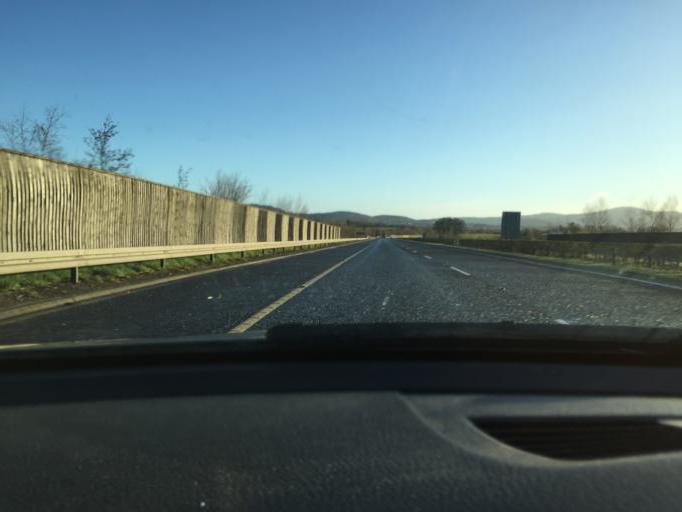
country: IE
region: Leinster
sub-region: Lu
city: Dundalk
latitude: 54.0264
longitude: -6.4360
